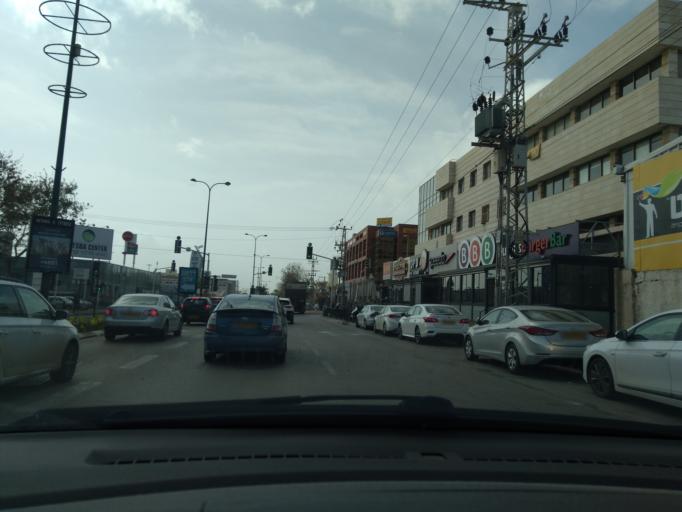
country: IL
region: Central District
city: Even Yehuda
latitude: 32.2785
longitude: 34.8603
